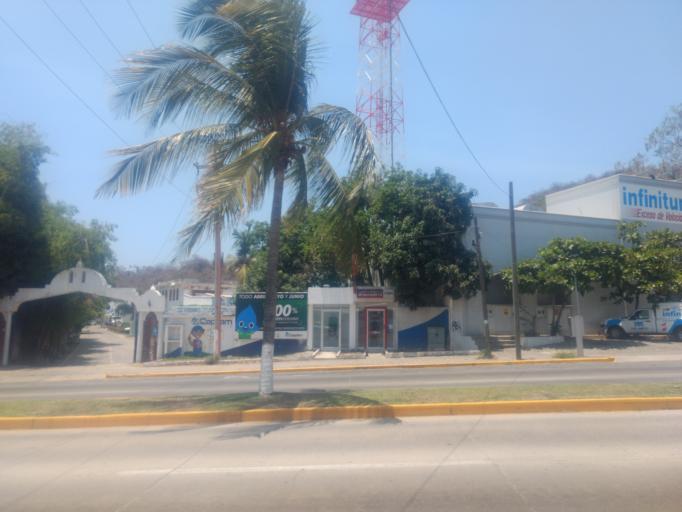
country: MX
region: Colima
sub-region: Manzanillo
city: Manzanillo
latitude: 19.1153
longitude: -104.3473
